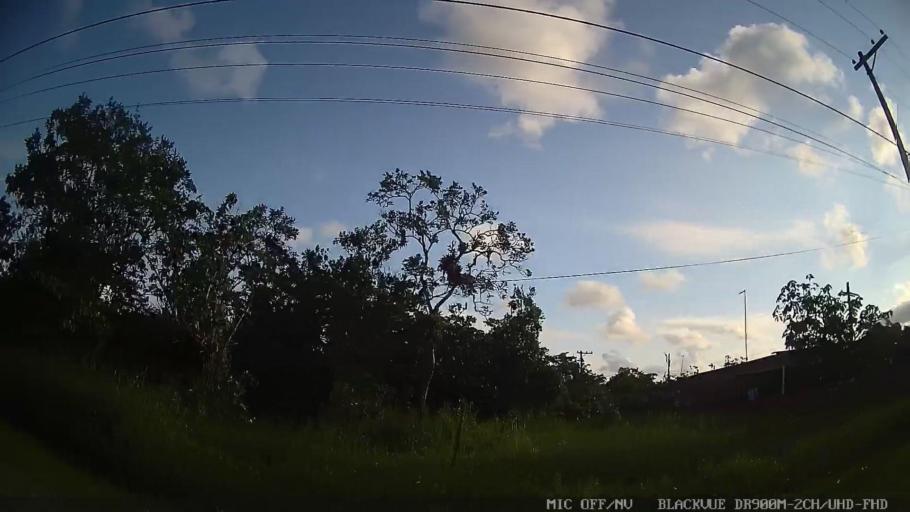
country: BR
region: Sao Paulo
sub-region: Itanhaem
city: Itanhaem
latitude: -24.1731
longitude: -46.8377
